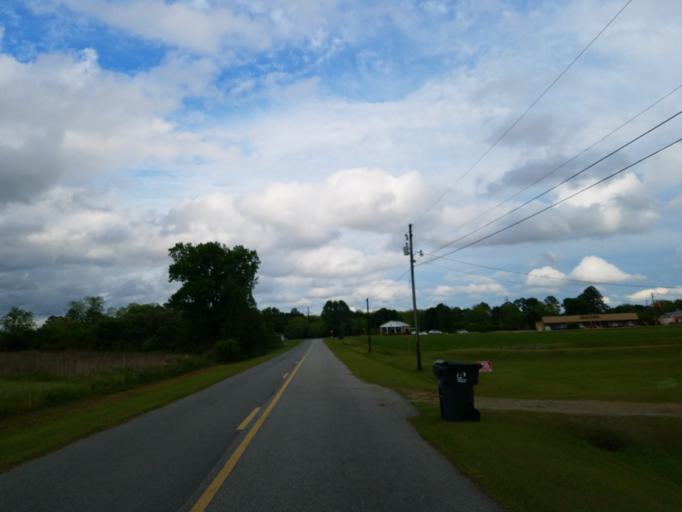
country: US
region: Georgia
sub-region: Dooly County
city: Unadilla
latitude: 32.2533
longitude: -83.7420
